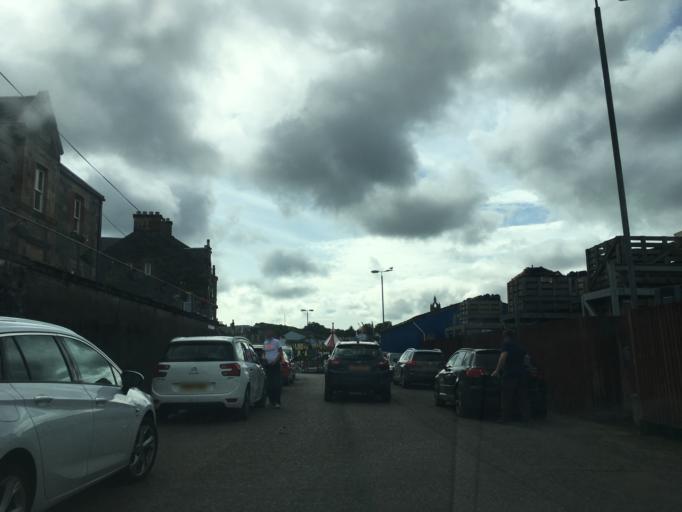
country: GB
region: Scotland
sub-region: Argyll and Bute
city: Tarbert
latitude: 55.8645
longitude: -5.4108
